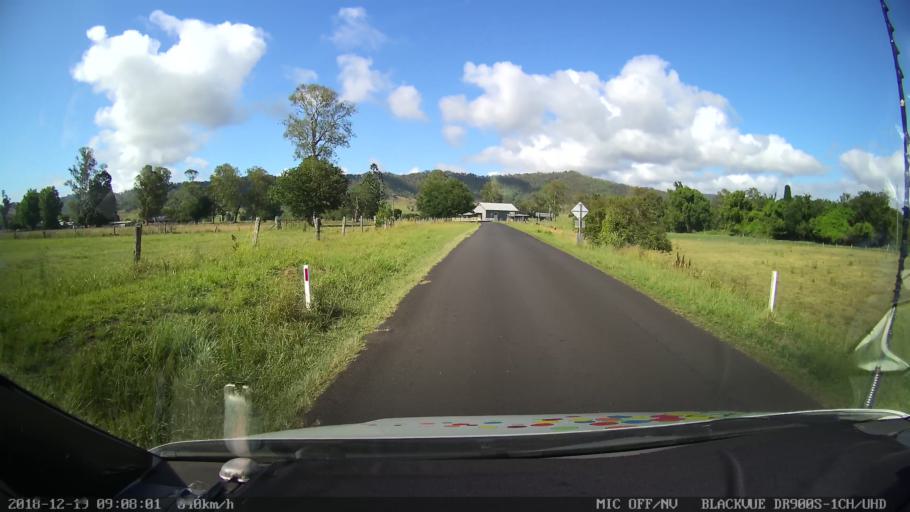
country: AU
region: New South Wales
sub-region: Kyogle
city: Kyogle
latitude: -28.4783
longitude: 152.9323
